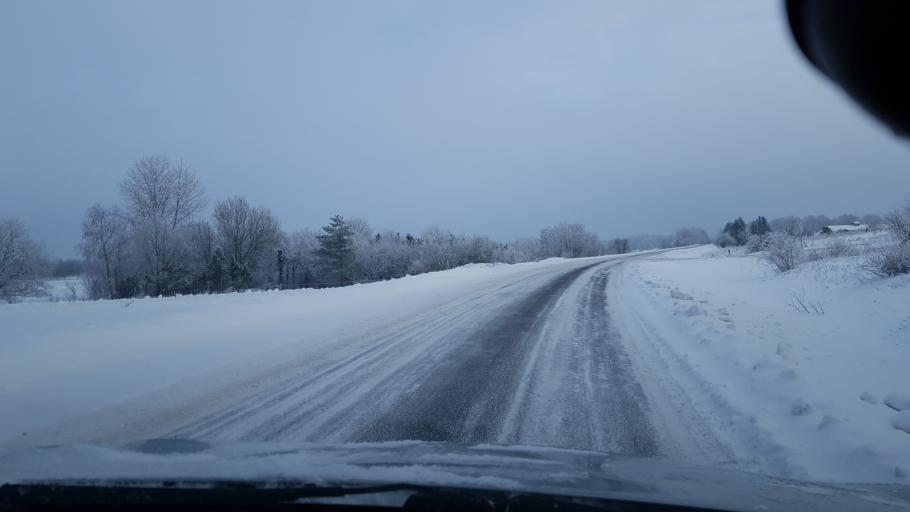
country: EE
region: Harju
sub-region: Keila linn
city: Keila
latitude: 59.3398
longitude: 24.4498
